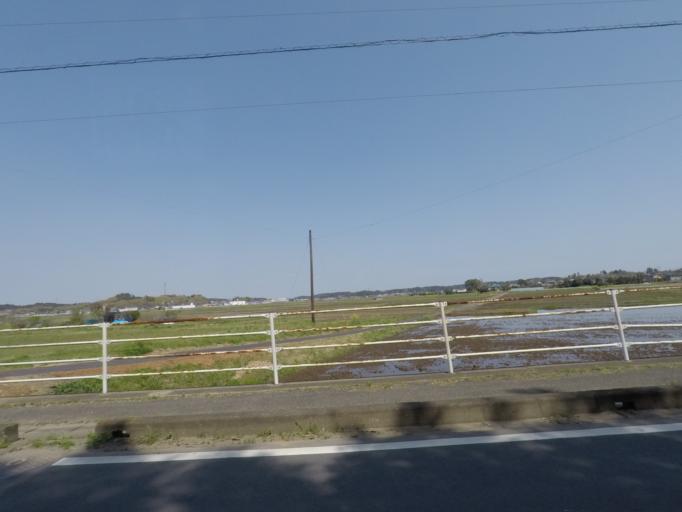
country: JP
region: Chiba
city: Yokaichiba
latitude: 35.7196
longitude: 140.4618
